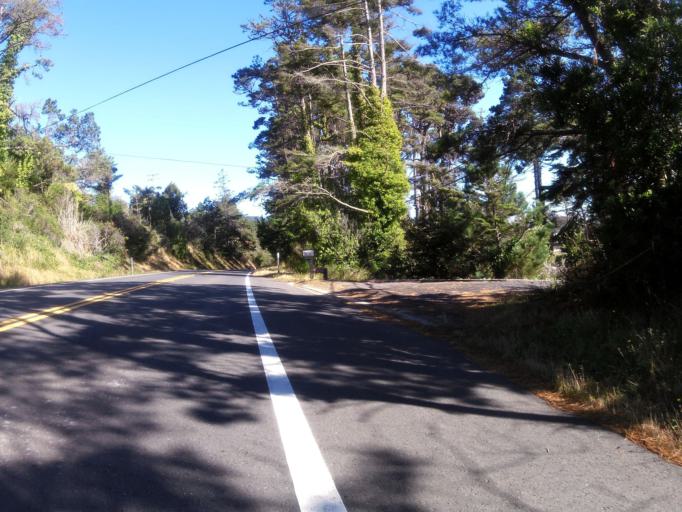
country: US
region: California
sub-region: Sonoma County
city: Sea Ranch
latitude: 38.8314
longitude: -123.6197
